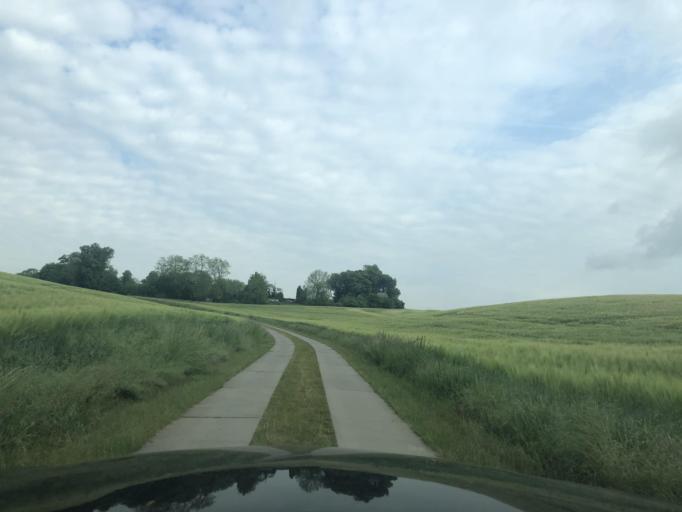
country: DE
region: Mecklenburg-Vorpommern
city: Trollenhagen
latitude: 53.6170
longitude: 13.2795
